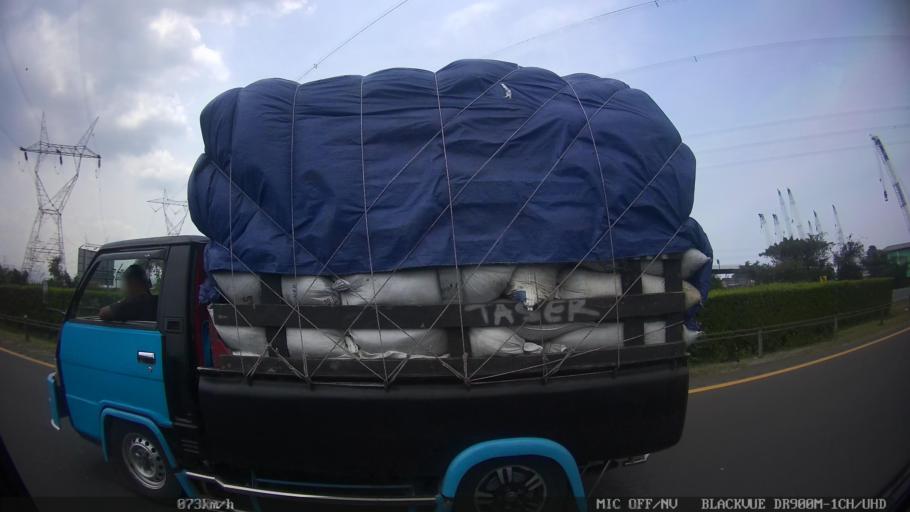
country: ID
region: Banten
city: Bojonegara
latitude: -6.0152
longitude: 106.0841
